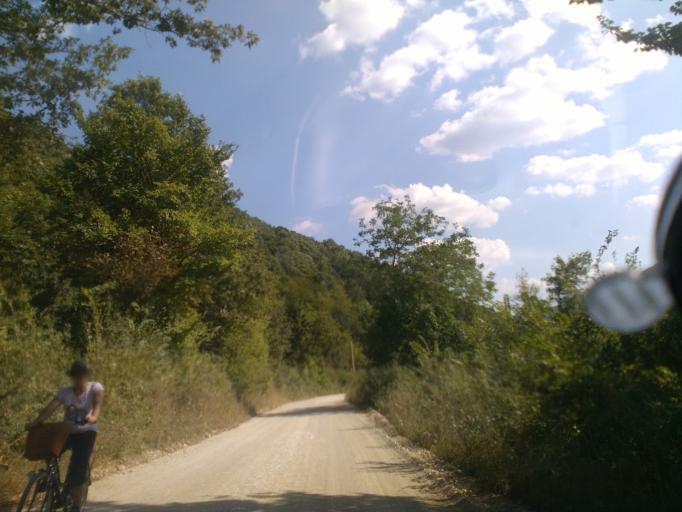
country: BA
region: Federation of Bosnia and Herzegovina
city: Orasac
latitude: 44.5150
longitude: 16.1274
